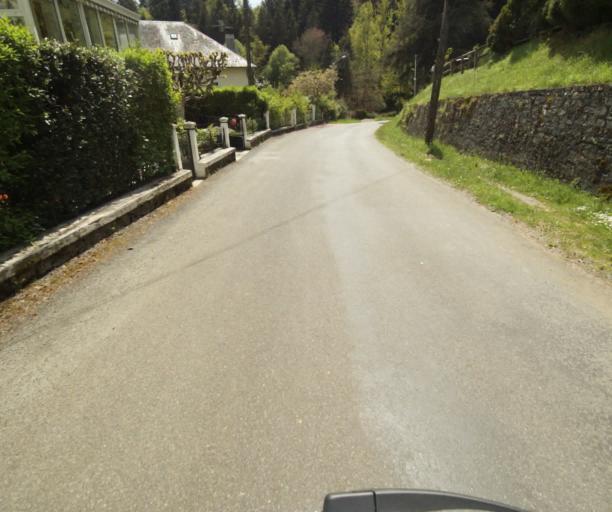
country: FR
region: Limousin
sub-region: Departement de la Correze
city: Tulle
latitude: 45.2768
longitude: 1.7581
